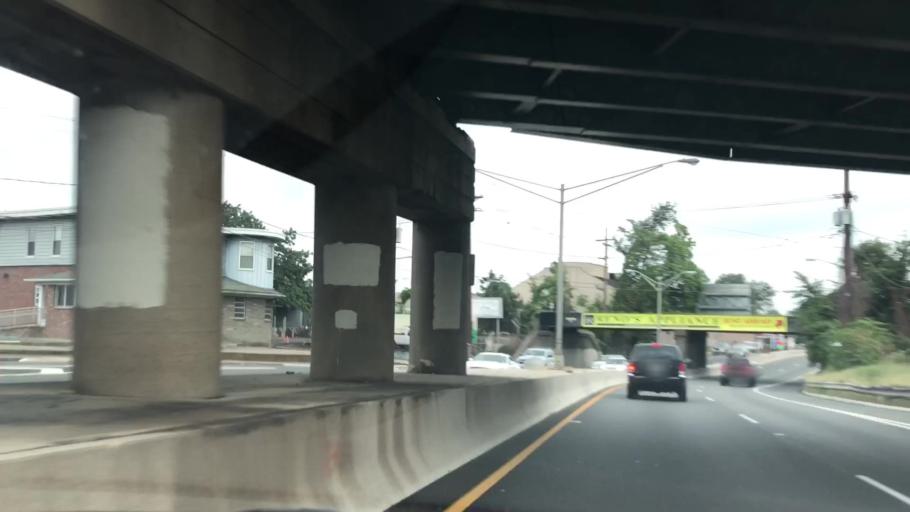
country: US
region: New Jersey
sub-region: Bergen County
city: Elmwood Park
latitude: 40.9036
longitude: -74.1351
